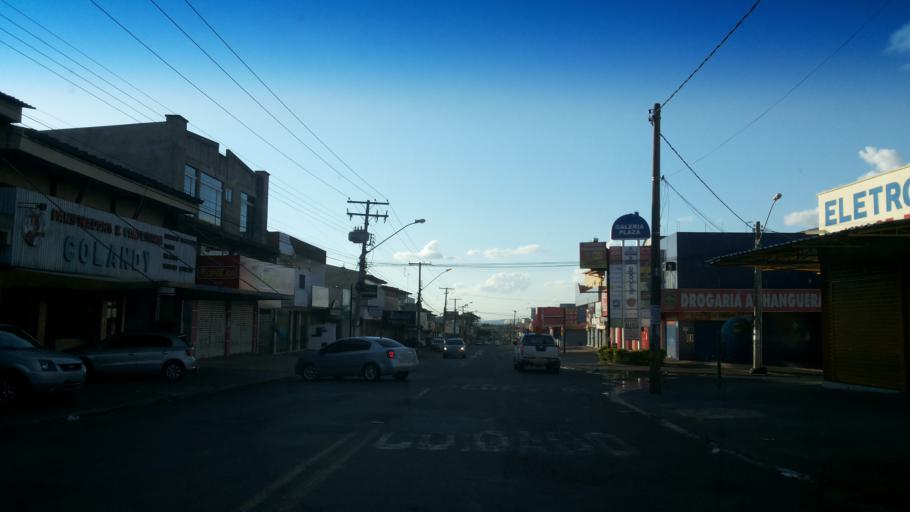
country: BR
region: Goias
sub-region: Goiania
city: Goiania
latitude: -16.7248
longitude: -49.3043
